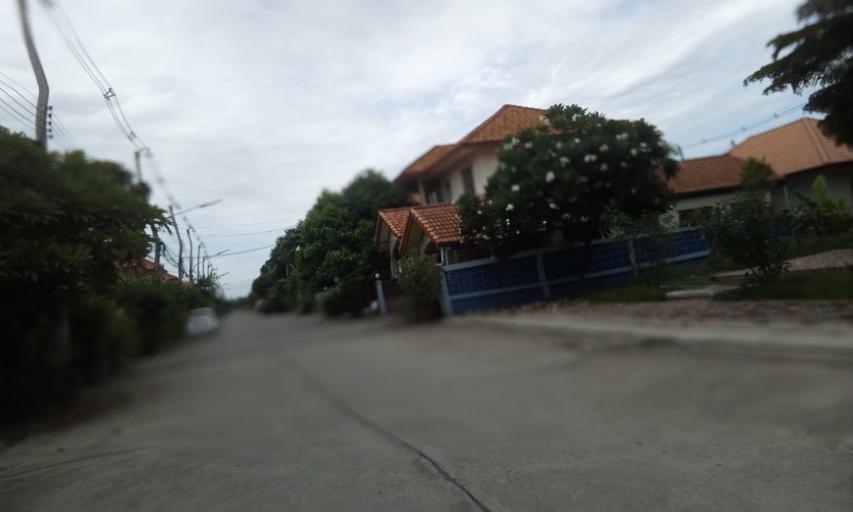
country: TH
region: Pathum Thani
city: Nong Suea
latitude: 14.0548
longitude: 100.8354
